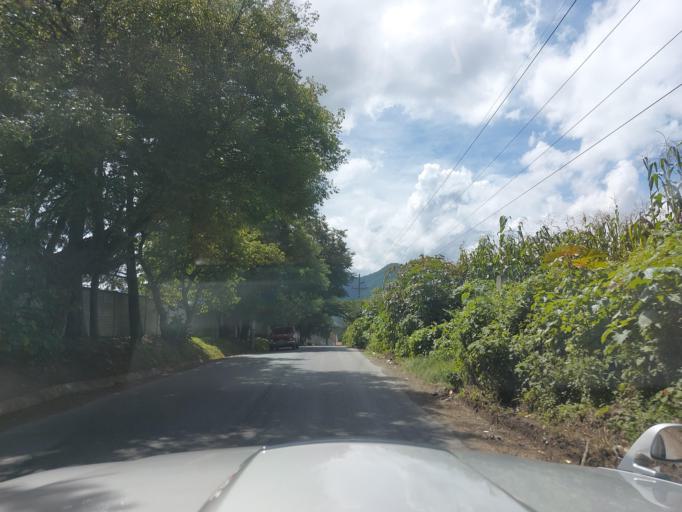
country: GT
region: Chimaltenango
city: Parramos
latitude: 14.6094
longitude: -90.8117
